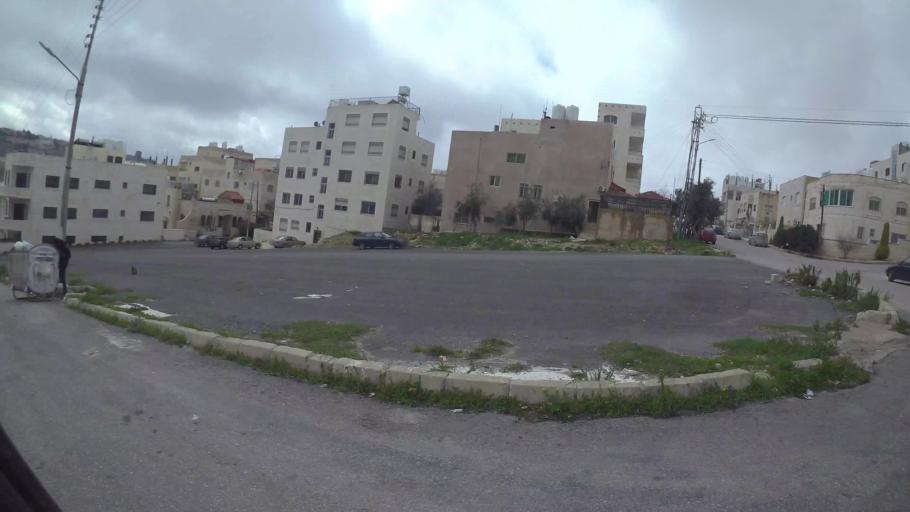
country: JO
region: Amman
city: Al Jubayhah
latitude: 32.0649
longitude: 35.8797
